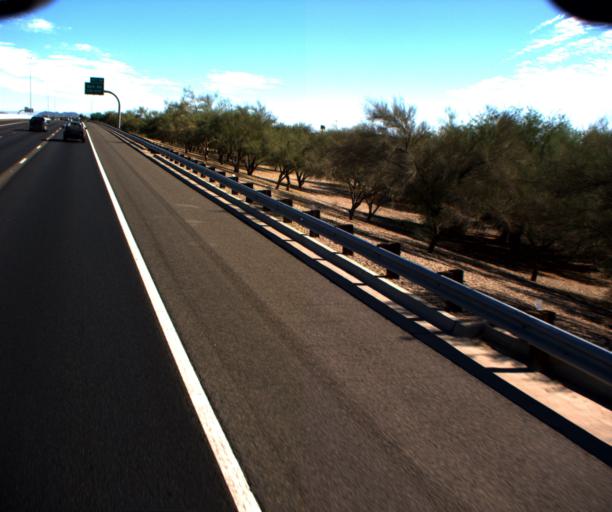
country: US
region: Arizona
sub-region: Maricopa County
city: Sun City
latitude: 33.6078
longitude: -112.2466
